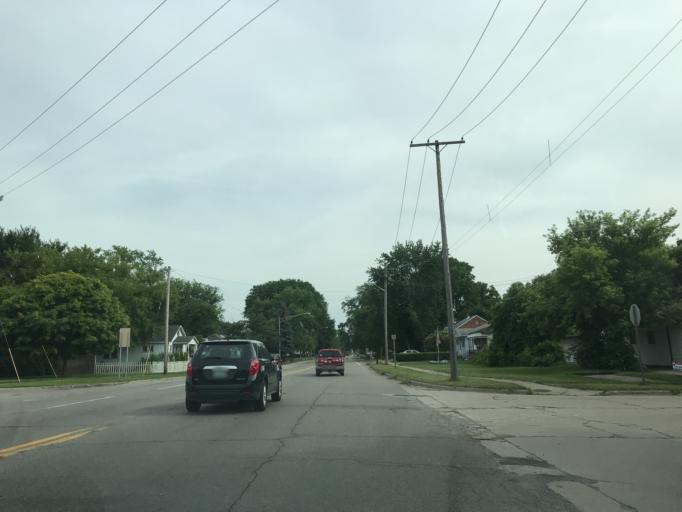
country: US
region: Michigan
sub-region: Wayne County
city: Redford
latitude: 42.4398
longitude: -83.3168
